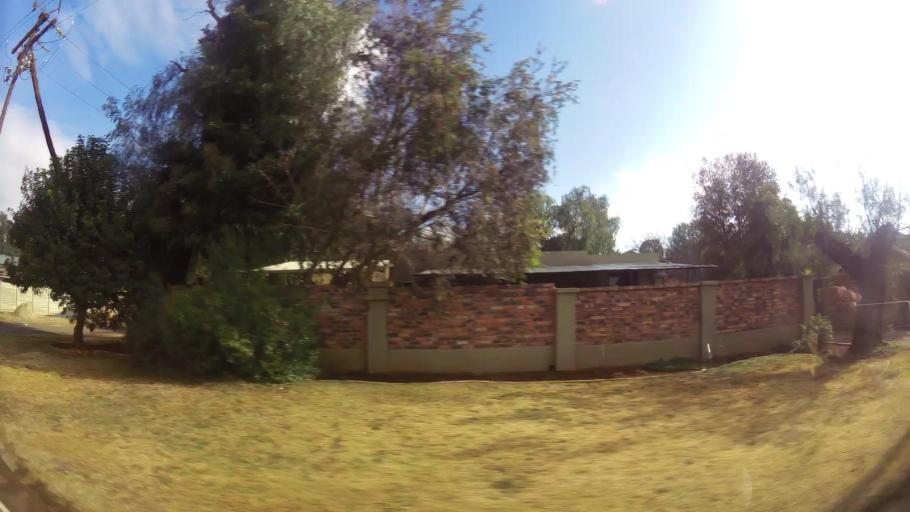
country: ZA
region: Gauteng
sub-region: Sedibeng District Municipality
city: Meyerton
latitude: -26.5502
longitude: 28.0589
